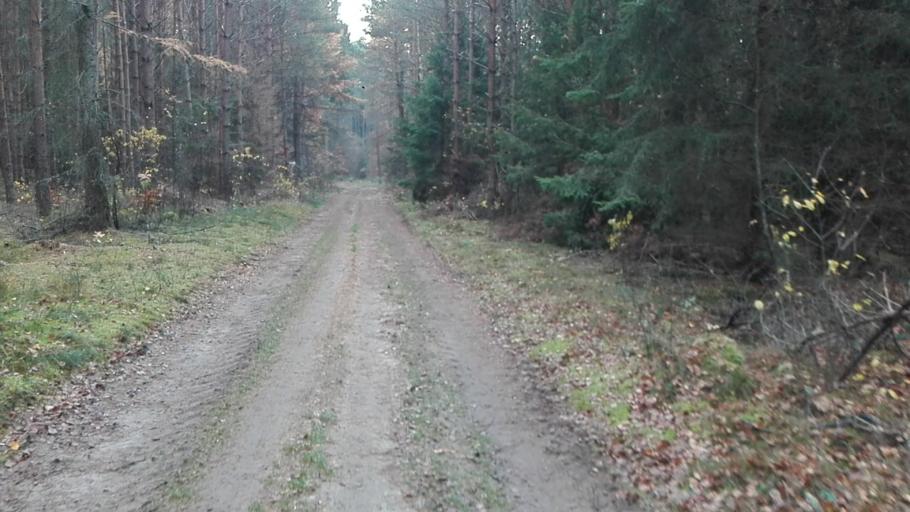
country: PL
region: West Pomeranian Voivodeship
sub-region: Powiat szczecinecki
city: Barwice
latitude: 53.8069
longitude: 16.3556
